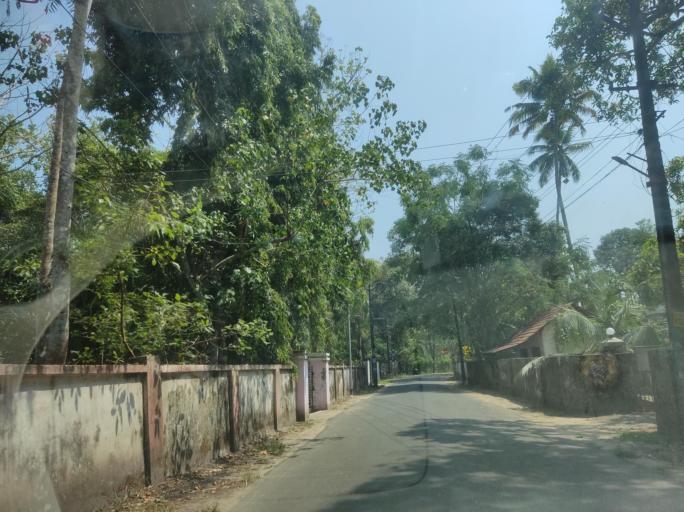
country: IN
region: Kerala
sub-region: Alappuzha
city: Vayalar
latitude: 9.6988
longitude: 76.3036
